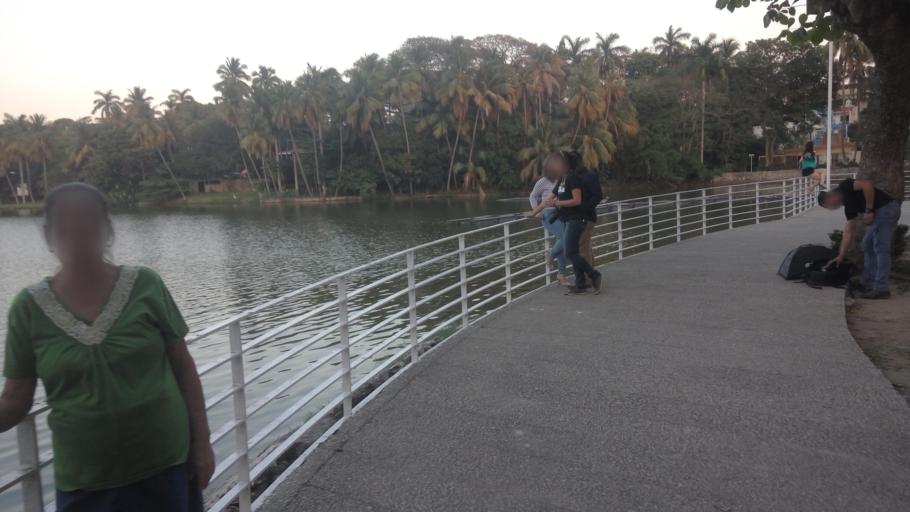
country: MX
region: Tabasco
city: Villahermosa
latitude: 17.9961
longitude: -92.9379
